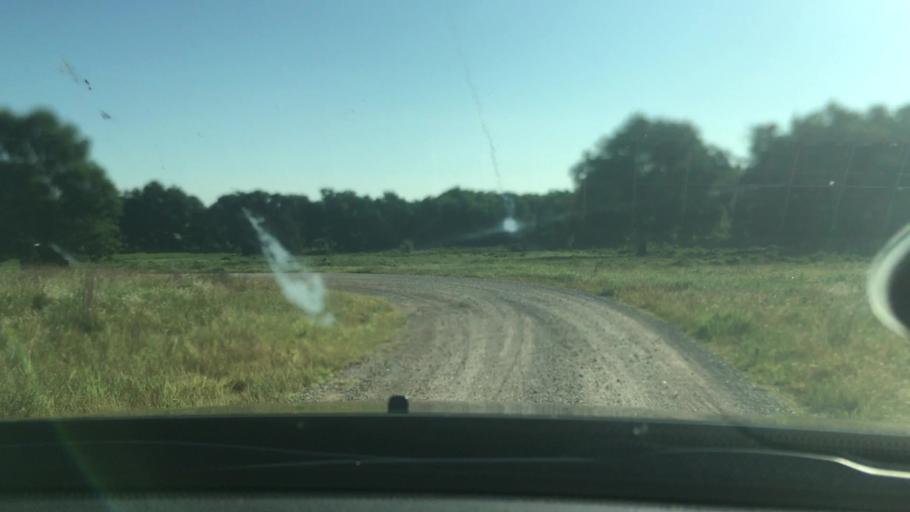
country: US
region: Oklahoma
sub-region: Johnston County
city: Tishomingo
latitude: 34.4173
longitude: -96.7602
